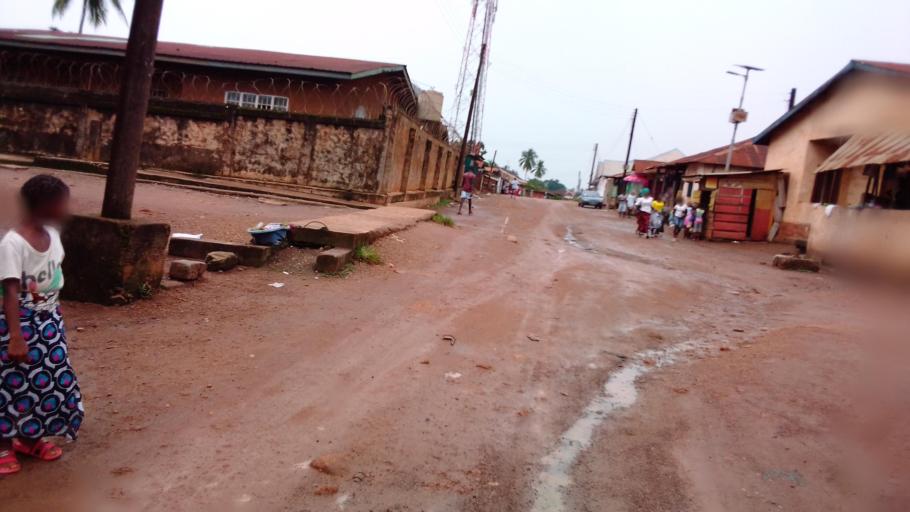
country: SL
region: Eastern Province
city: Kenema
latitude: 7.8681
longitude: -11.1928
